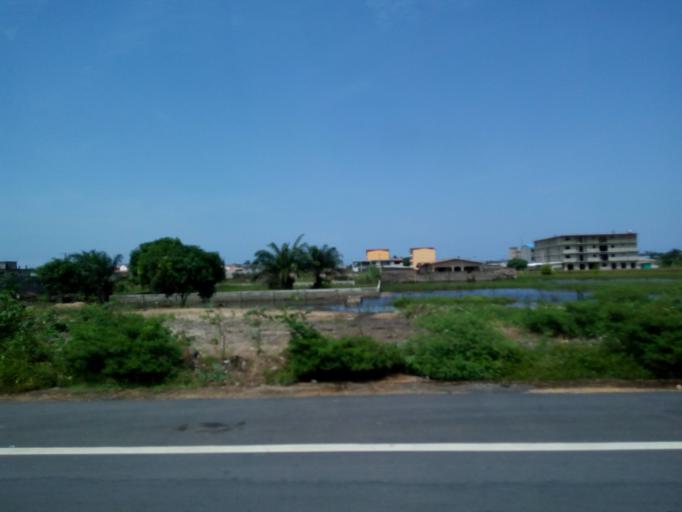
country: CI
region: Sud-Comoe
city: Grand-Bassam
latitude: 5.2252
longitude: -3.7343
